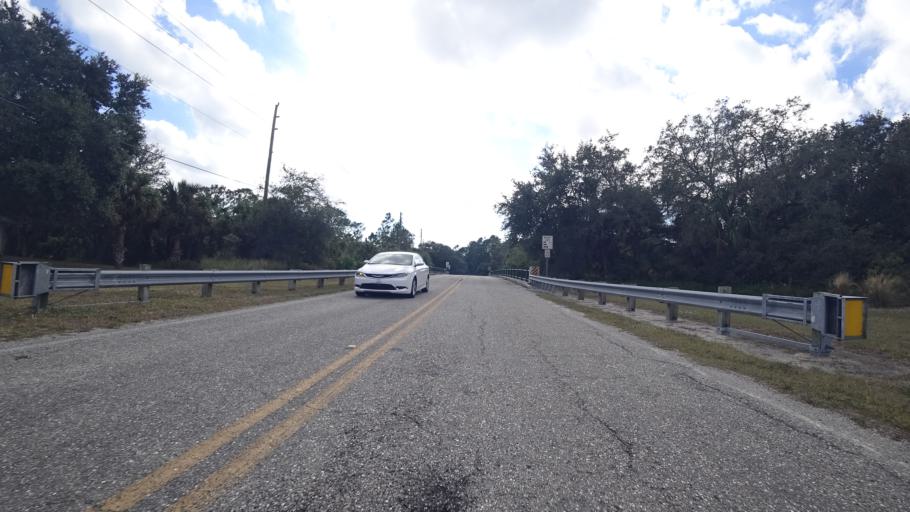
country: US
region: Florida
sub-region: Charlotte County
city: Port Charlotte
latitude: 27.0336
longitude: -82.1337
